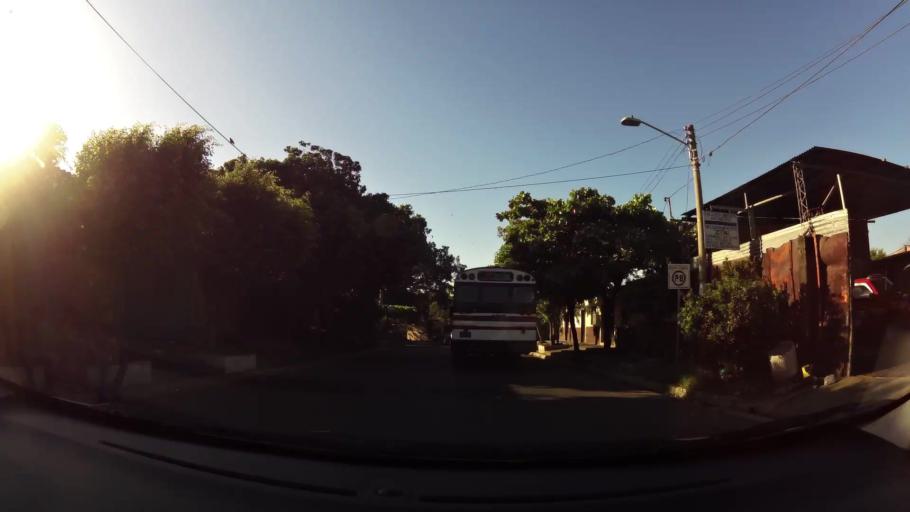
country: SV
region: Sonsonate
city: San Antonio del Monte
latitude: 13.7132
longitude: -89.7336
